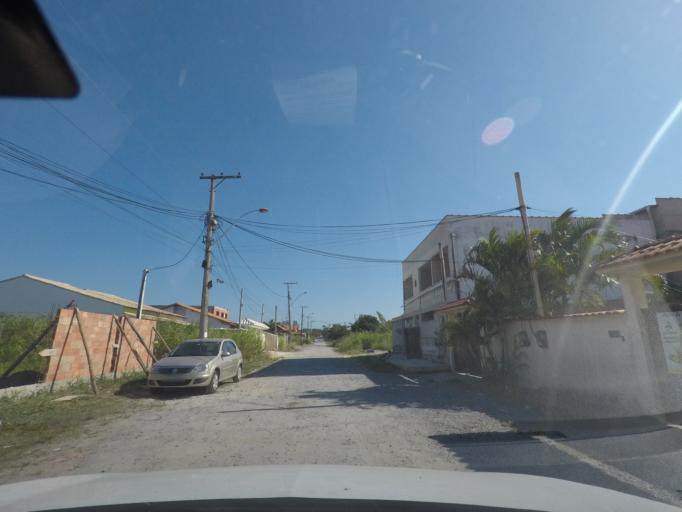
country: BR
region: Rio de Janeiro
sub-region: Marica
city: Marica
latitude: -22.9655
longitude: -42.9226
